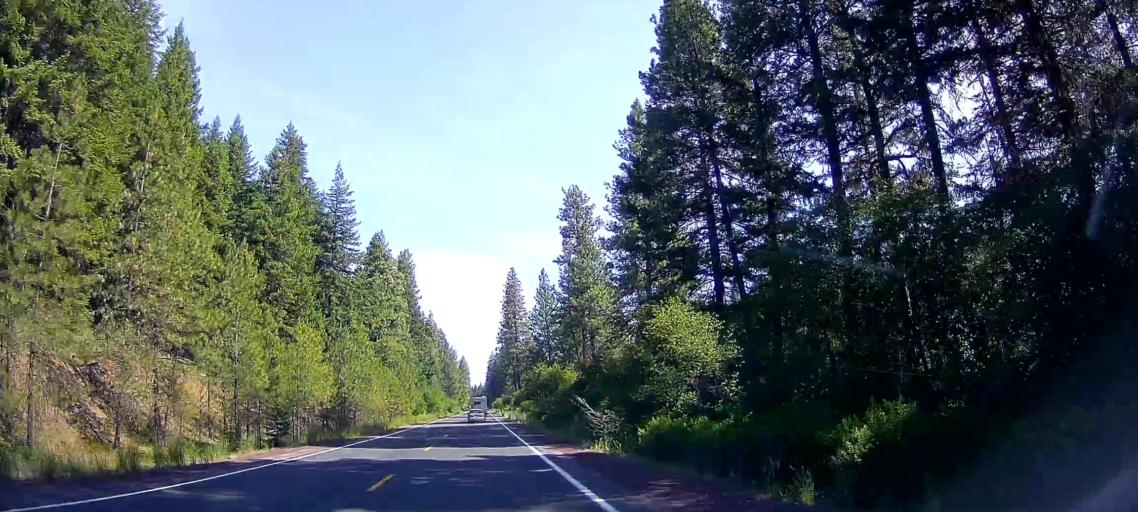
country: US
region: Oregon
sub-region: Jefferson County
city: Warm Springs
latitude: 45.0381
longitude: -121.5105
